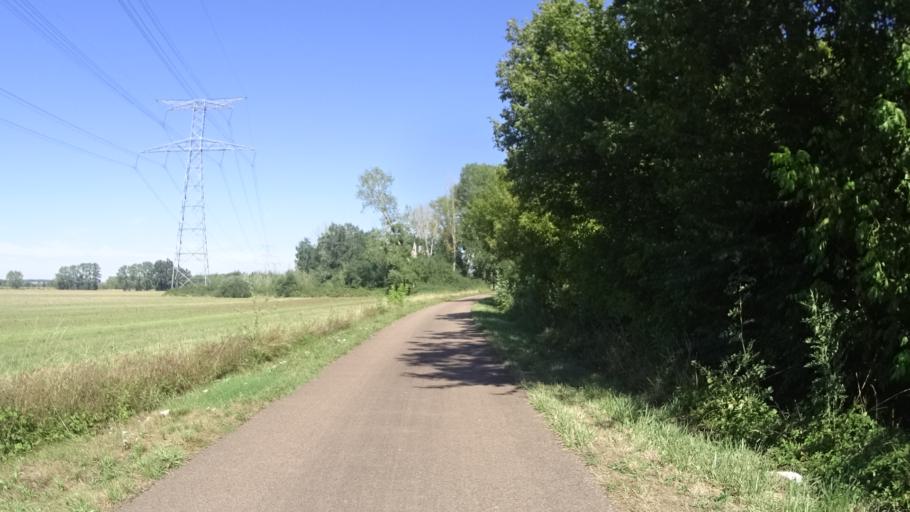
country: FR
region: Bourgogne
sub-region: Departement de la Nievre
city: Neuvy-sur-Loire
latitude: 47.4934
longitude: 2.8905
